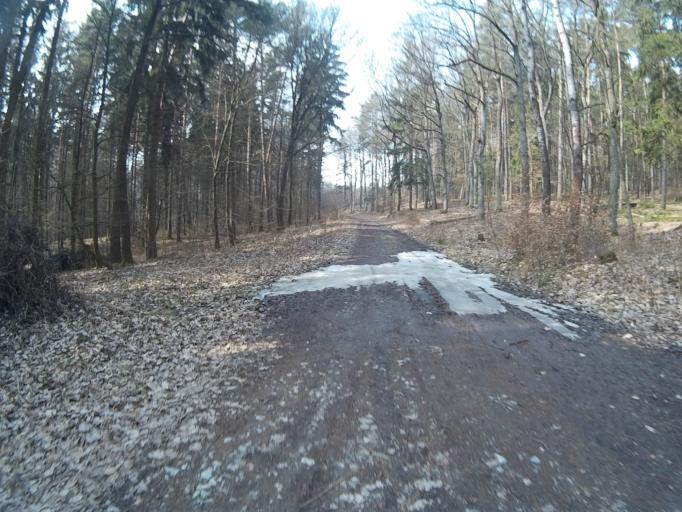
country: CZ
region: South Moravian
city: Pozorice
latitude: 49.2267
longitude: 16.8001
